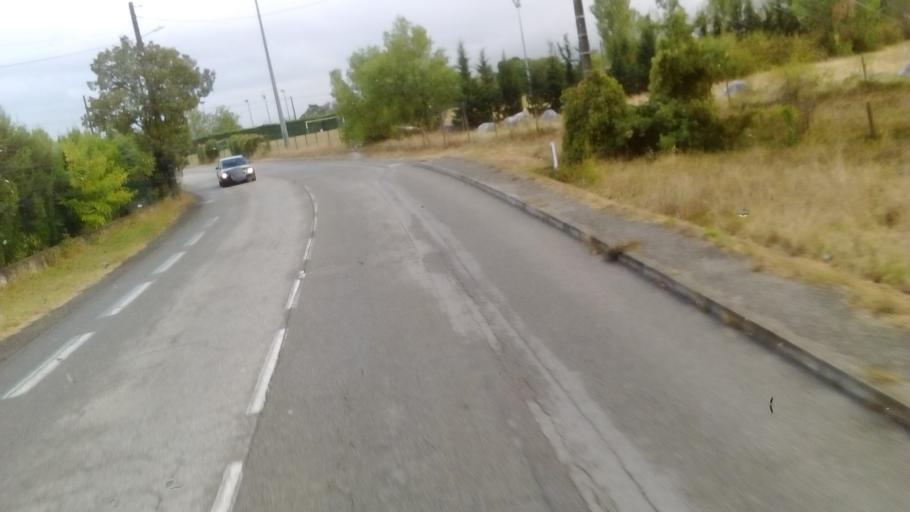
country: FR
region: Rhone-Alpes
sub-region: Departement de l'Ardeche
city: Cornas
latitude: 44.9650
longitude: 4.8746
